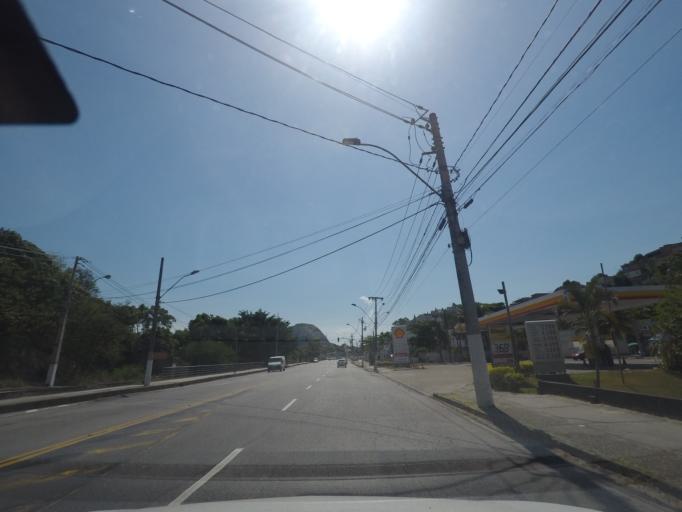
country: BR
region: Rio de Janeiro
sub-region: Niteroi
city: Niteroi
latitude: -22.9113
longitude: -43.0566
